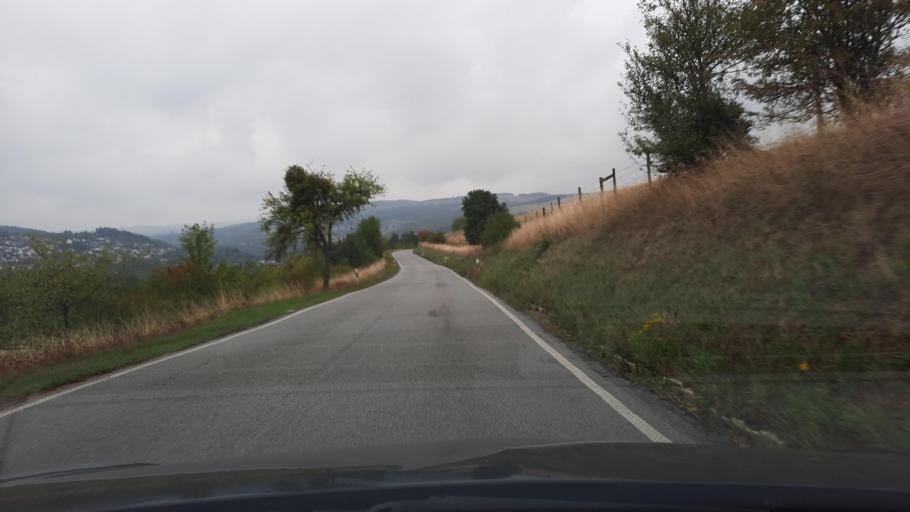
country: DE
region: Rheinland-Pfalz
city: Pluwig
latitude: 49.6879
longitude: 6.7051
